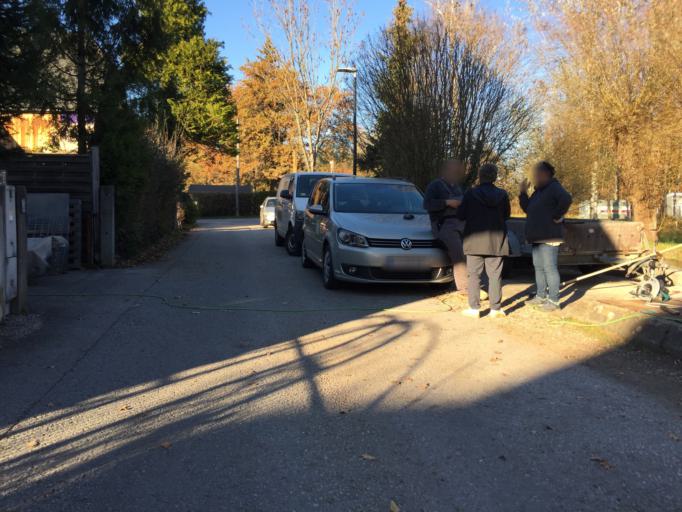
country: AT
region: Salzburg
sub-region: Politischer Bezirk Salzburg-Umgebung
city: Anif
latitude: 47.7654
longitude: 13.0393
